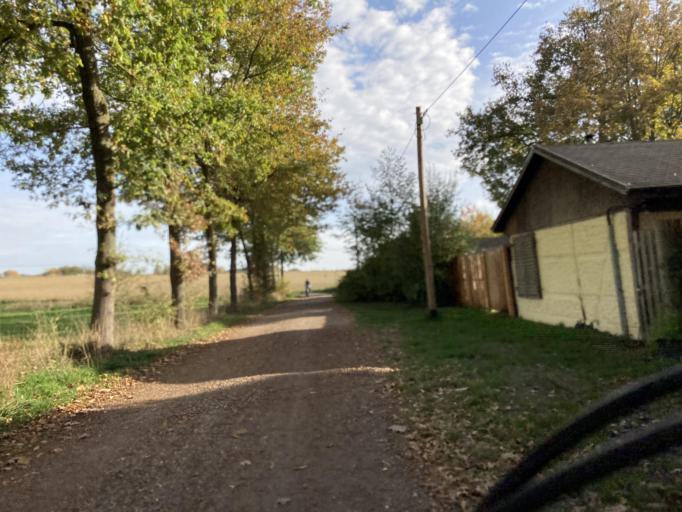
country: DE
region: North Rhine-Westphalia
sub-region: Regierungsbezirk Munster
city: Muenster
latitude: 51.9731
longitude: 7.7017
